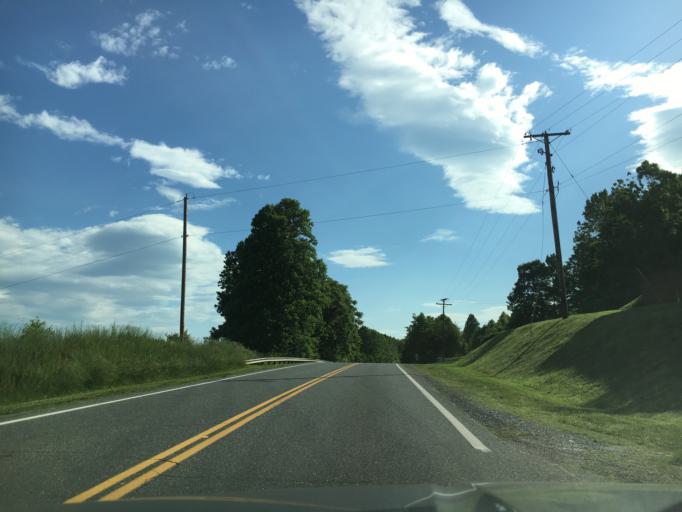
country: US
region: Virginia
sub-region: City of Lynchburg
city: West Lynchburg
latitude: 37.3530
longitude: -79.1725
